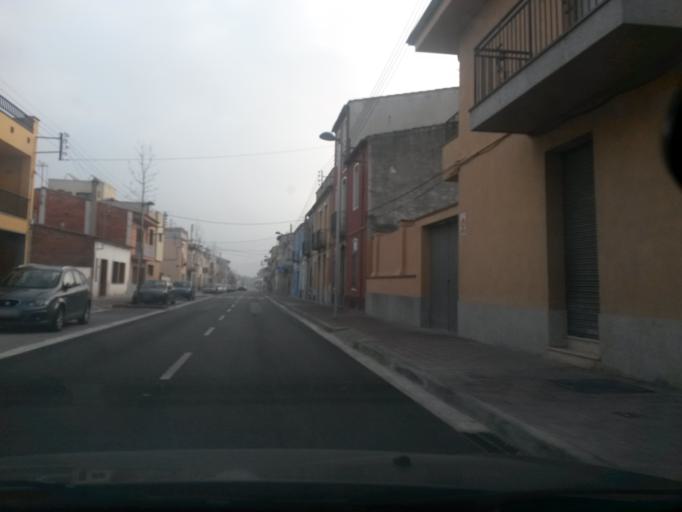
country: ES
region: Catalonia
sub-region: Provincia de Girona
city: Llagostera
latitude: 41.8288
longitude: 2.8975
